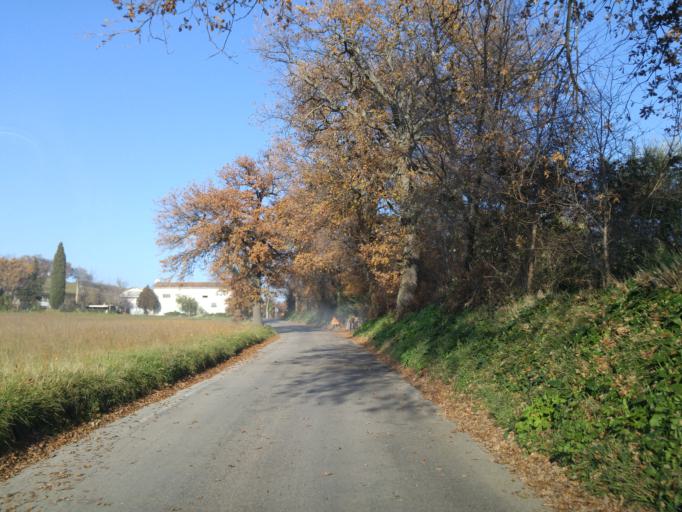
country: IT
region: The Marches
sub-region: Provincia di Pesaro e Urbino
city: Montefelcino
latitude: 43.7268
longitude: 12.8447
